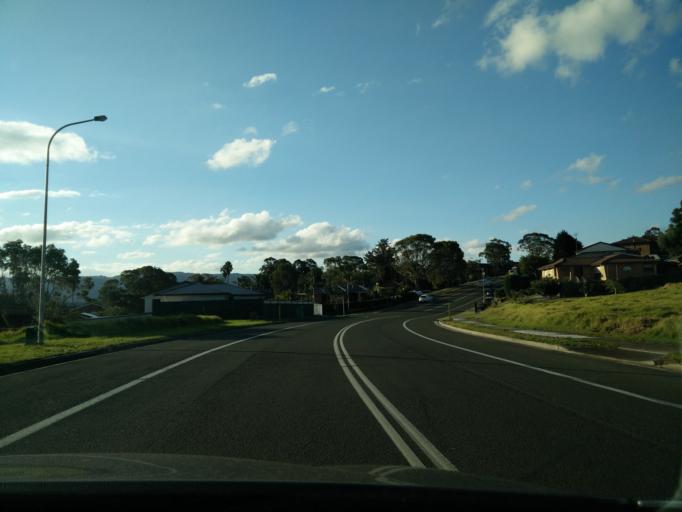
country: AU
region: New South Wales
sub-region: Wollongong
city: Berkeley
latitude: -34.4700
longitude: 150.8440
